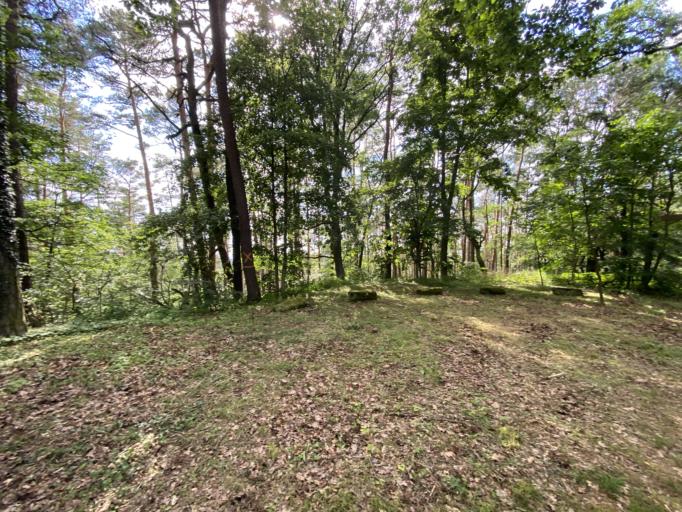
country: DE
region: Bavaria
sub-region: Regierungsbezirk Mittelfranken
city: Bubenreuth
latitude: 49.6186
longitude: 11.0194
